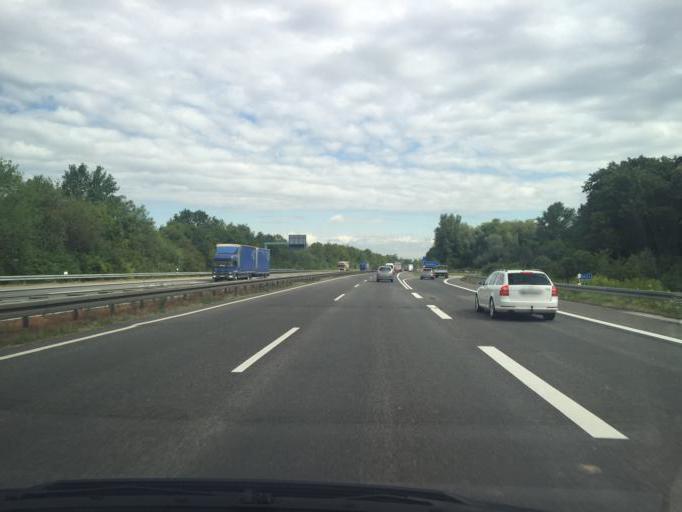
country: DE
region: Hesse
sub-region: Regierungsbezirk Darmstadt
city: Bensheim
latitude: 49.6727
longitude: 8.6003
